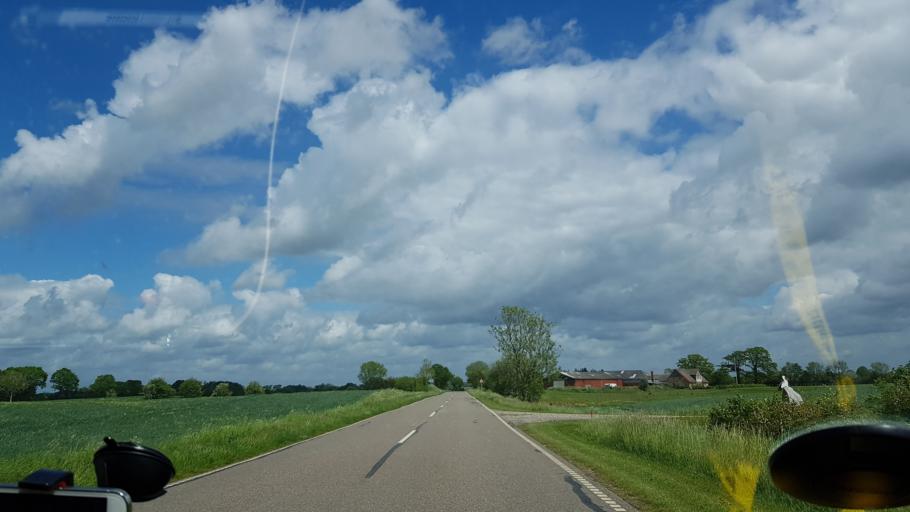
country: DK
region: South Denmark
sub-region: Kolding Kommune
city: Christiansfeld
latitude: 55.3365
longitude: 9.4567
